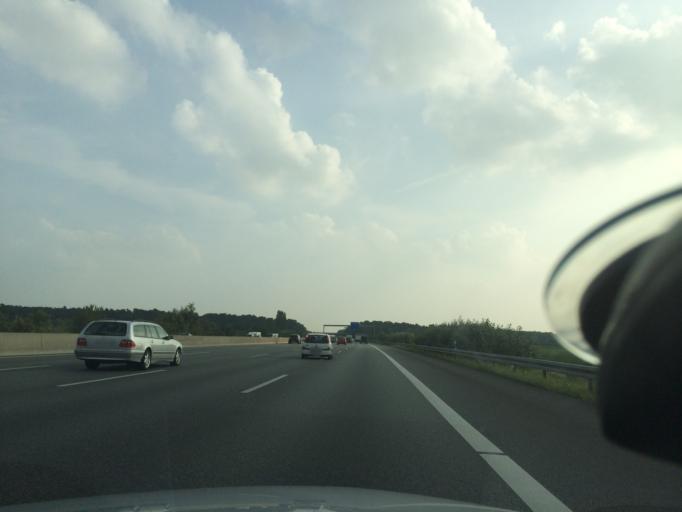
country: DE
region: Hesse
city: Weiterstadt
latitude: 49.9159
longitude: 8.6095
